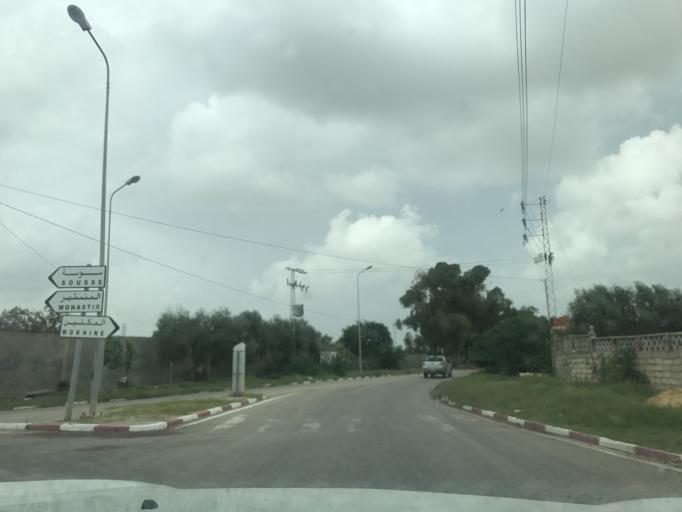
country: TN
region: Al Munastir
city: Qasr Hallal
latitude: 35.6025
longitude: 10.8991
